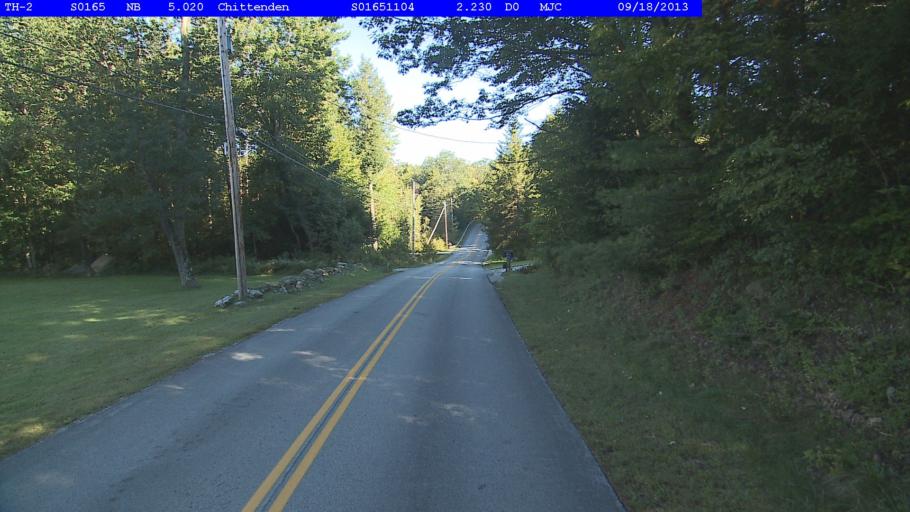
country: US
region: Vermont
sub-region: Rutland County
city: Rutland
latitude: 43.7078
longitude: -72.9615
